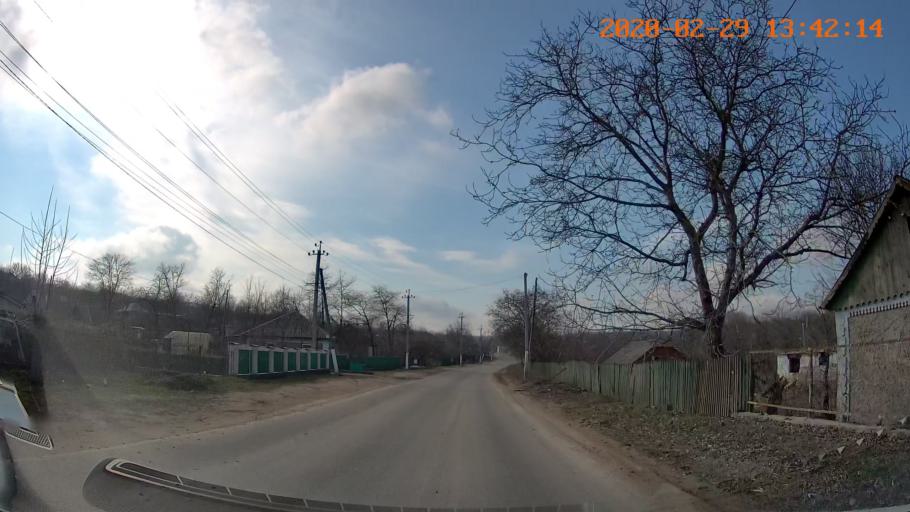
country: MD
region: Floresti
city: Leninskiy
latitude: 47.8420
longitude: 28.5506
